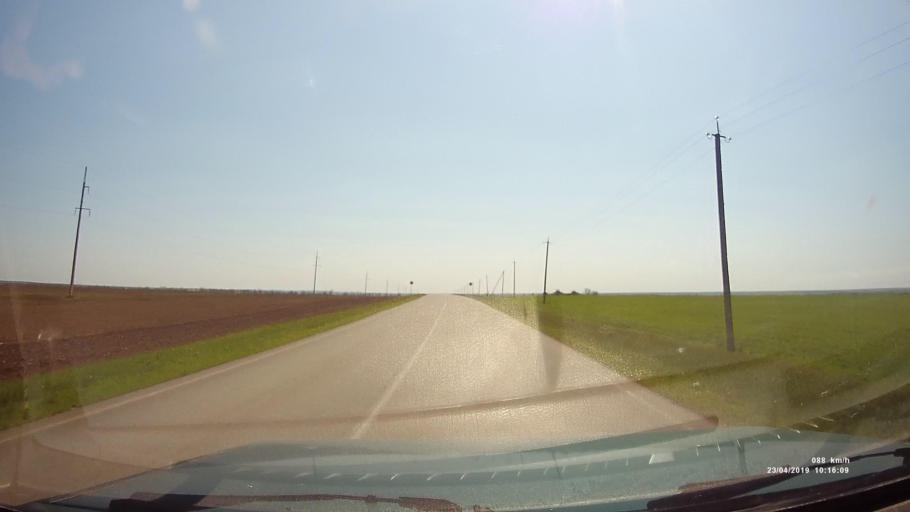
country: RU
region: Rostov
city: Sovetskoye
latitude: 46.6603
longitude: 42.3908
